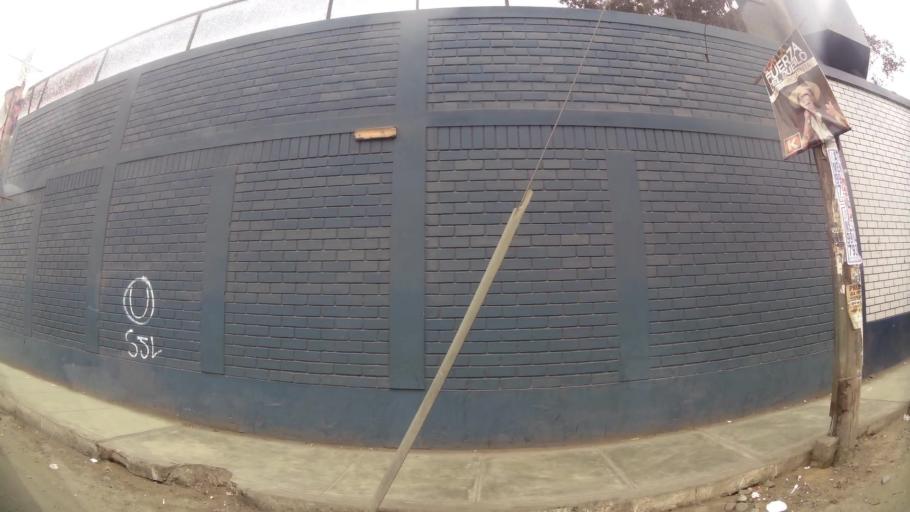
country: PE
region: Lima
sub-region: Lima
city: La Molina
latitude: -12.0528
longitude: -76.9605
